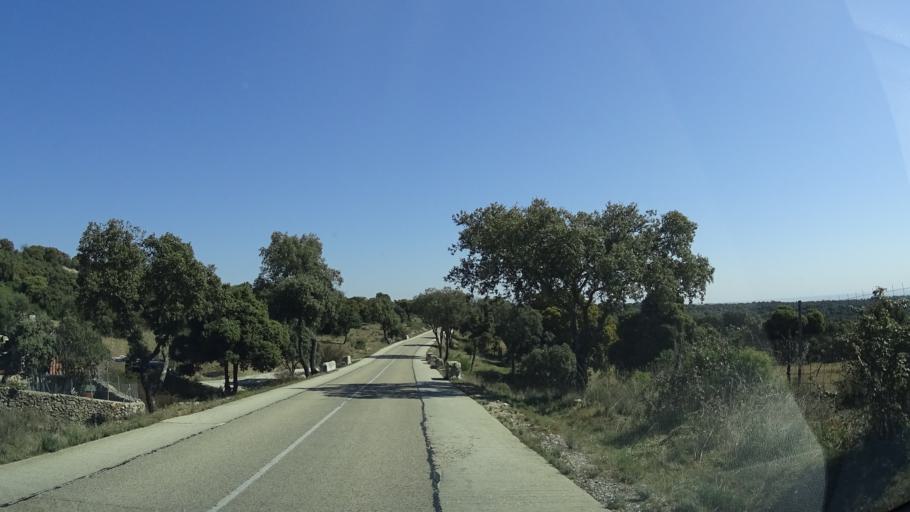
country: ES
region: Madrid
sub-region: Provincia de Madrid
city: Hoyo de Manzanares
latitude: 40.6381
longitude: -3.8506
